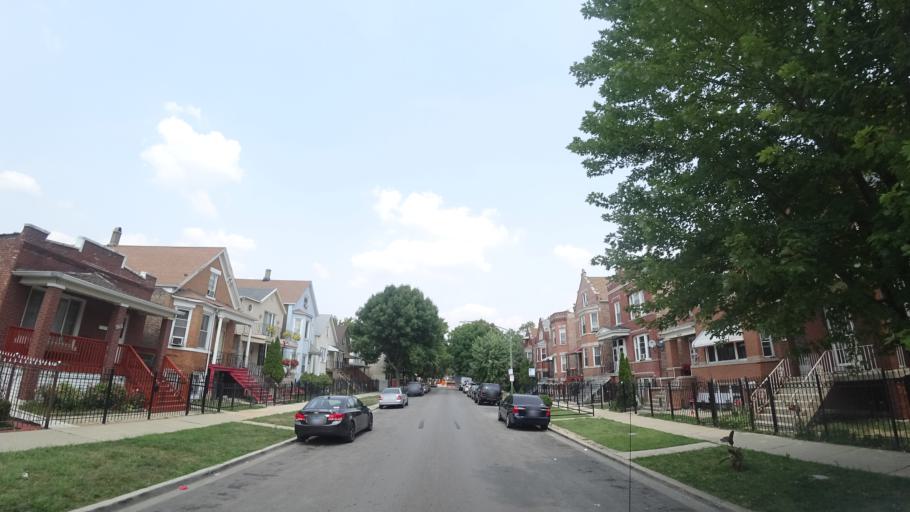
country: US
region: Illinois
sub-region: Cook County
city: Cicero
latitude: 41.8378
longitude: -87.7305
